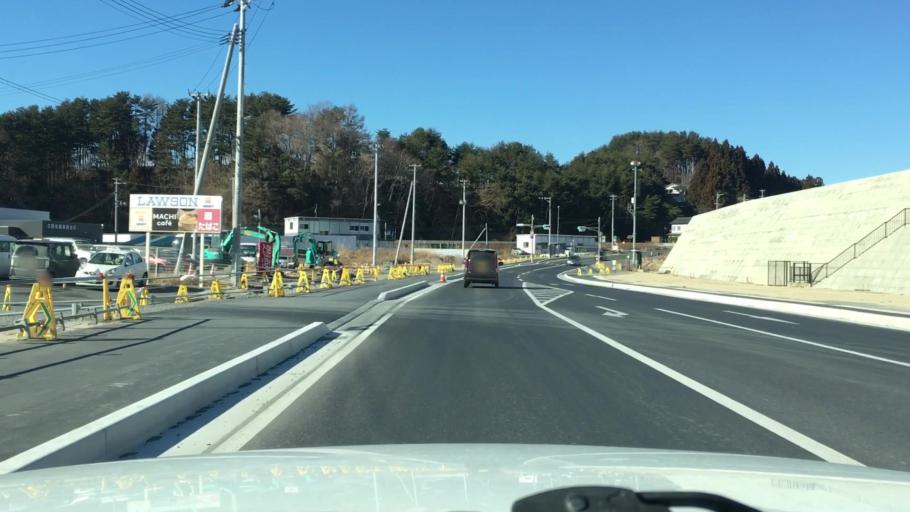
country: JP
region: Iwate
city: Yamada
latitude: 39.4562
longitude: 141.9576
